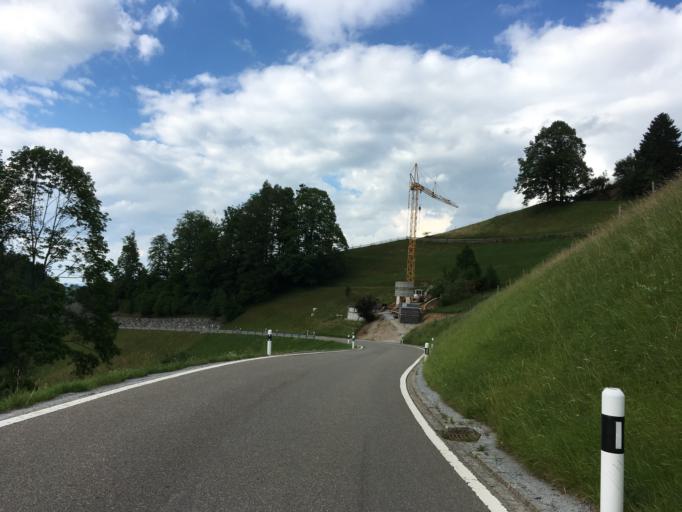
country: CH
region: Saint Gallen
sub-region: Wahlkreis Toggenburg
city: Lichtensteig
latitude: 47.3223
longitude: 9.0658
